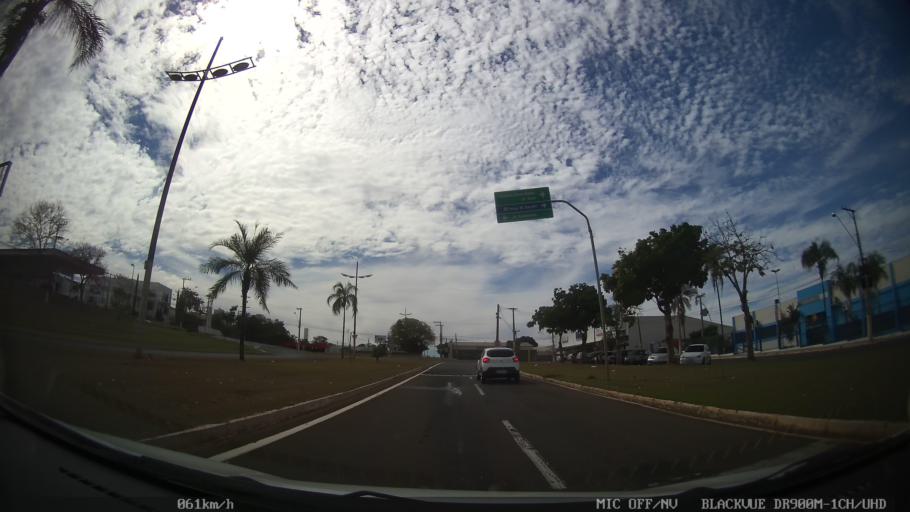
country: BR
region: Sao Paulo
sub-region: Catanduva
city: Catanduva
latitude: -21.1518
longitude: -48.9803
